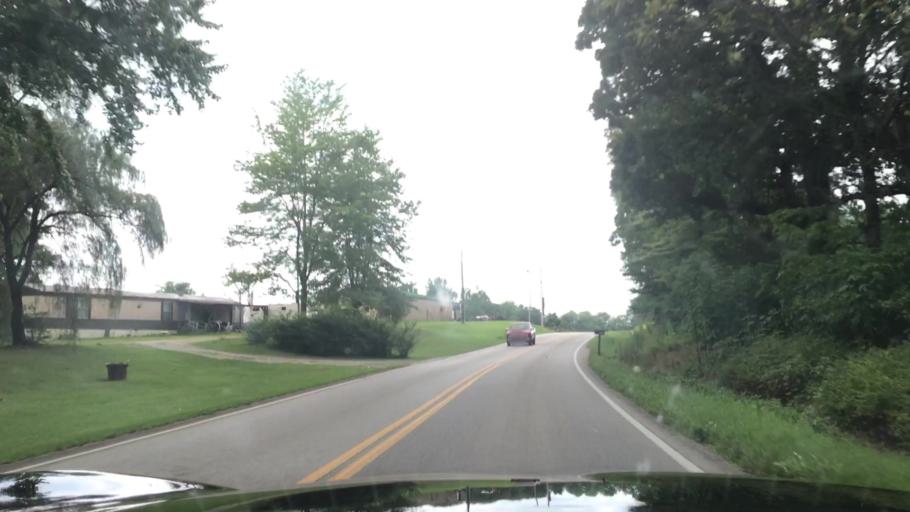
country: US
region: Kentucky
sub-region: Butler County
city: Morgantown
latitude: 37.1743
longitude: -86.8077
